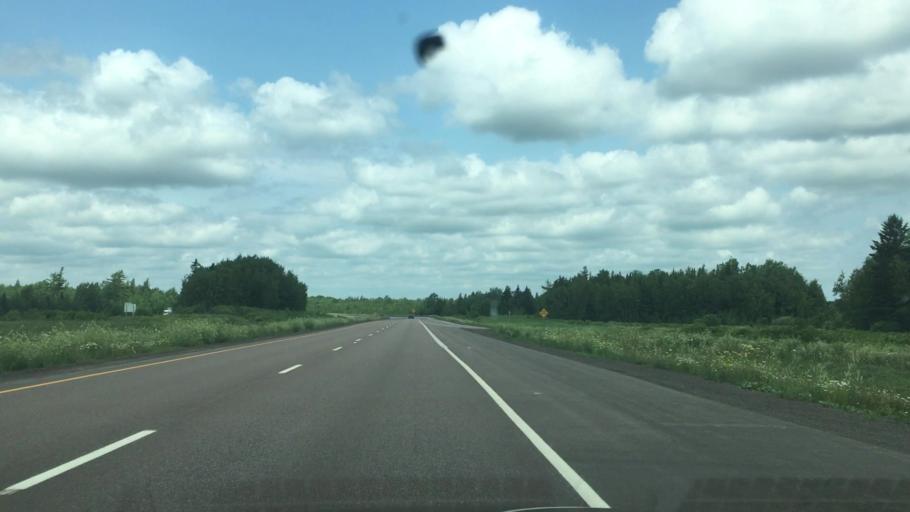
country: CA
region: New Brunswick
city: Dieppe
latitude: 46.1036
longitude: -64.6073
